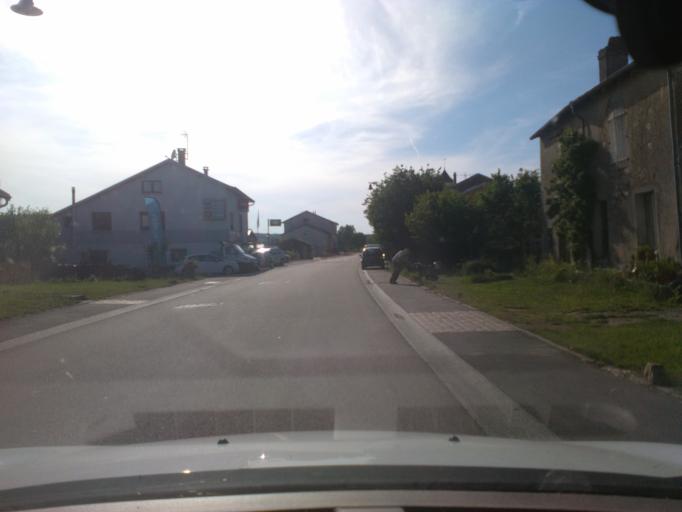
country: FR
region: Lorraine
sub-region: Departement des Vosges
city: Mirecourt
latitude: 48.2624
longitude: 6.1740
